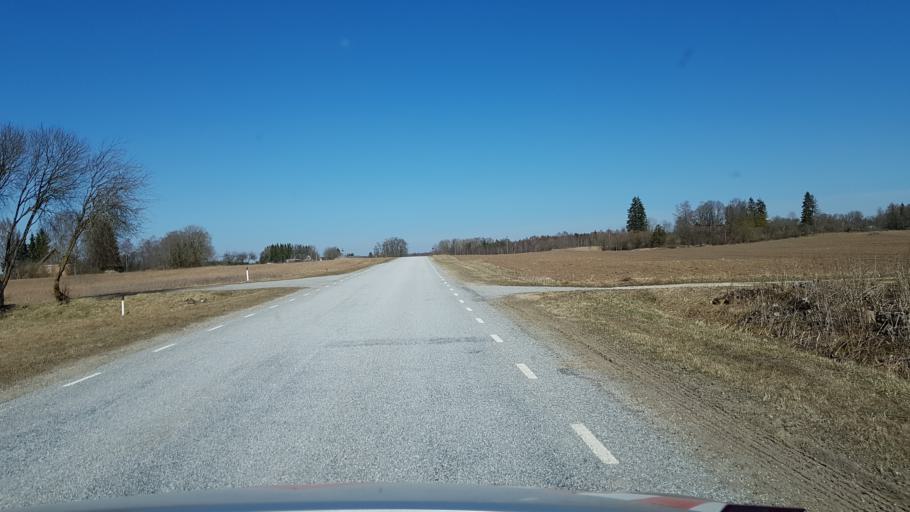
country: EE
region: Jaervamaa
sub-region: Koeru vald
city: Koeru
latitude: 59.0332
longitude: 26.0910
